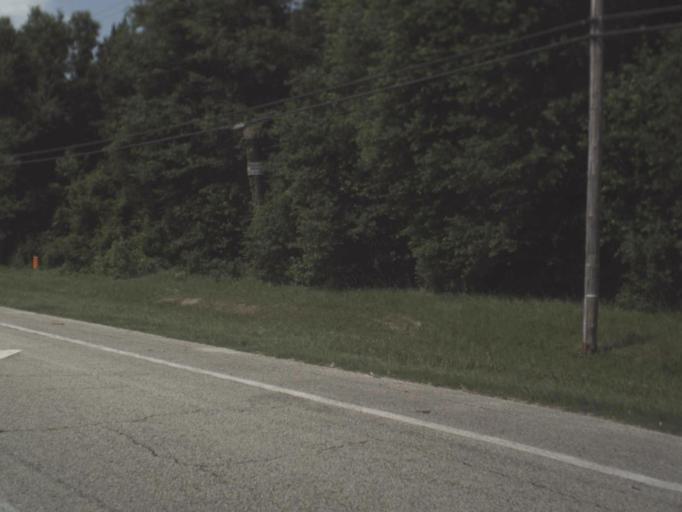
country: US
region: Florida
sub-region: Alachua County
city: Hawthorne
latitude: 29.6202
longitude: -82.0970
